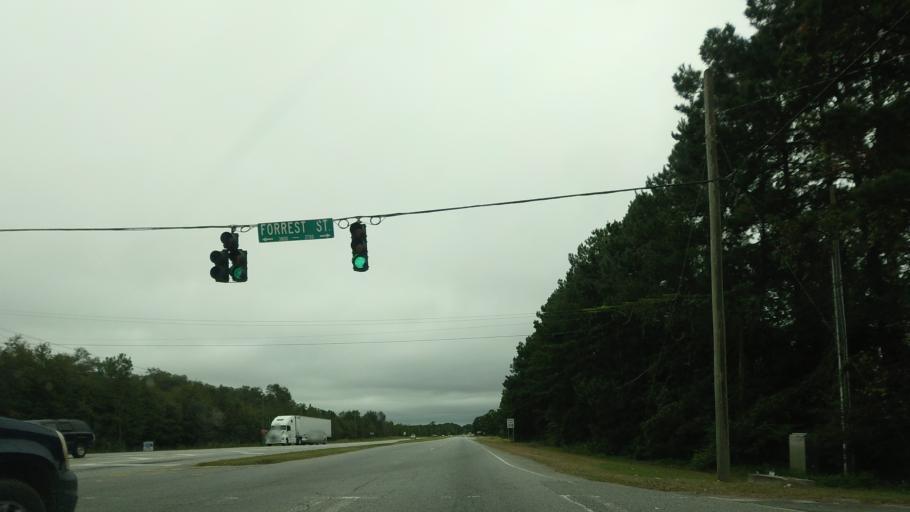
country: US
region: Georgia
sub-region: Lowndes County
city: Valdosta
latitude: 30.8827
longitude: -83.2657
